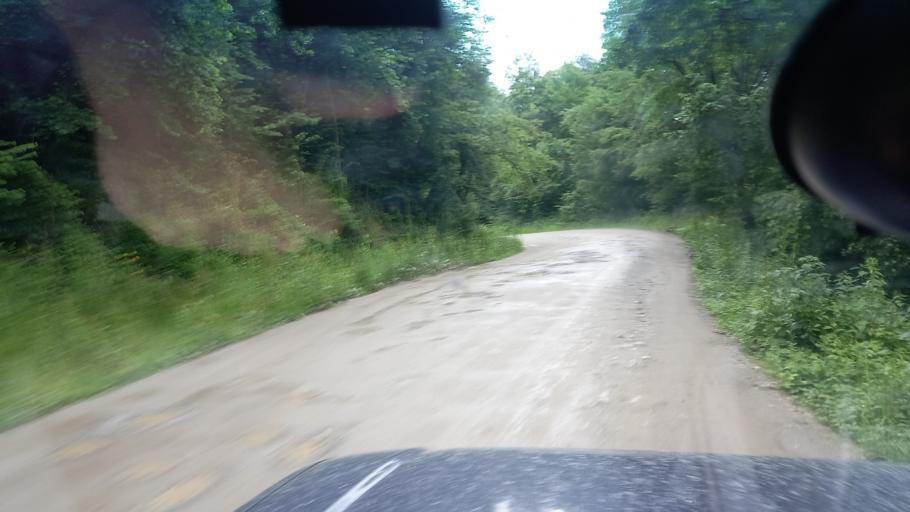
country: RU
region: Krasnodarskiy
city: Psebay
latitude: 44.0320
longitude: 40.7411
